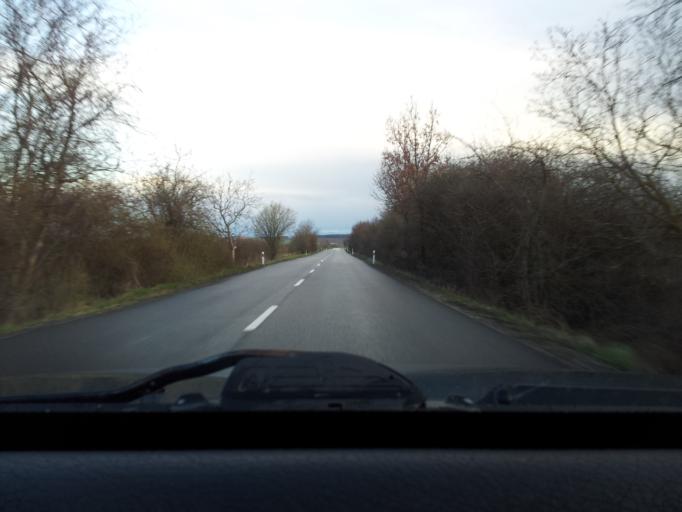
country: SK
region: Nitriansky
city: Tlmace
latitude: 48.3361
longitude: 18.4905
